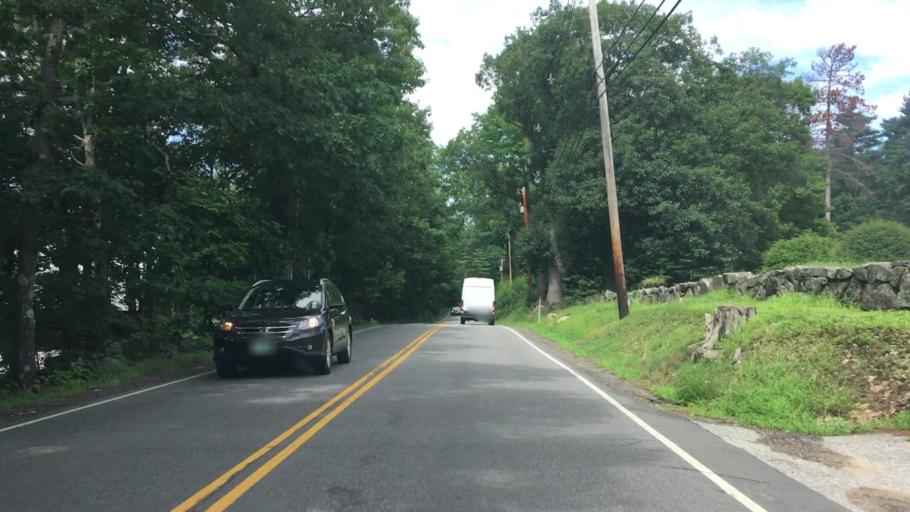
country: US
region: New Hampshire
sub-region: Belknap County
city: Meredith
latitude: 43.6187
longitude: -71.5399
